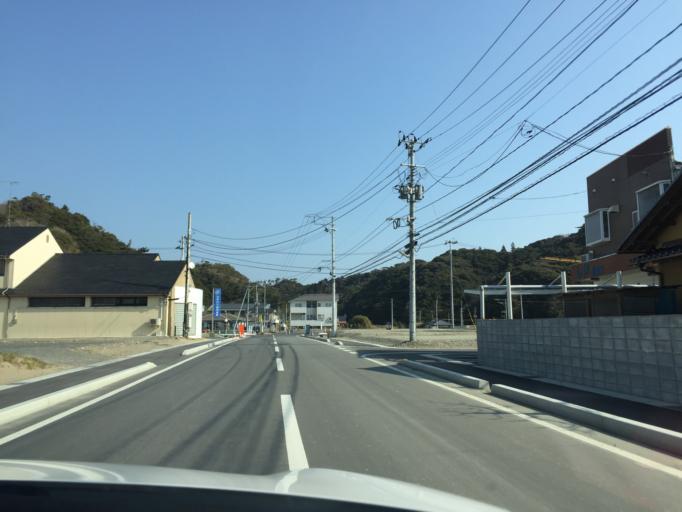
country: JP
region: Fukushima
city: Iwaki
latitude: 36.9926
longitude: 140.9714
